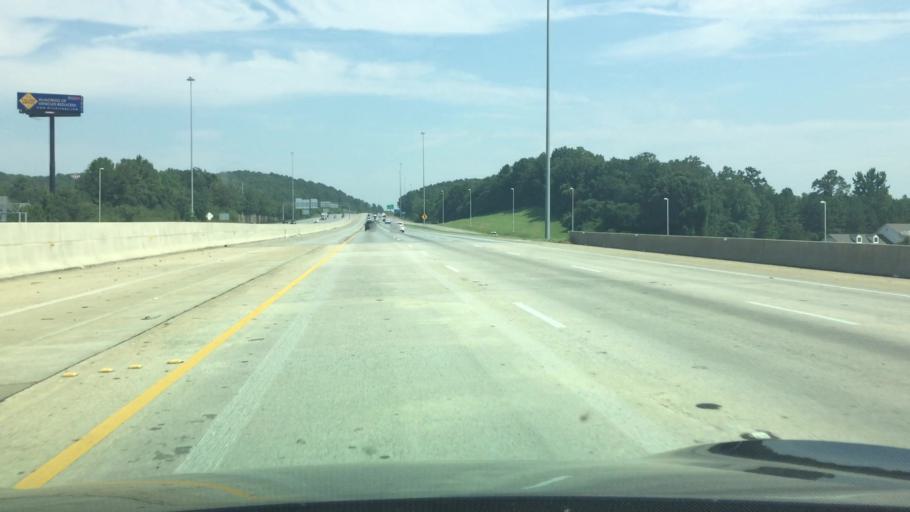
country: US
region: Alabama
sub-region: Shelby County
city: Indian Springs Village
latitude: 33.3369
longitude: -86.7797
